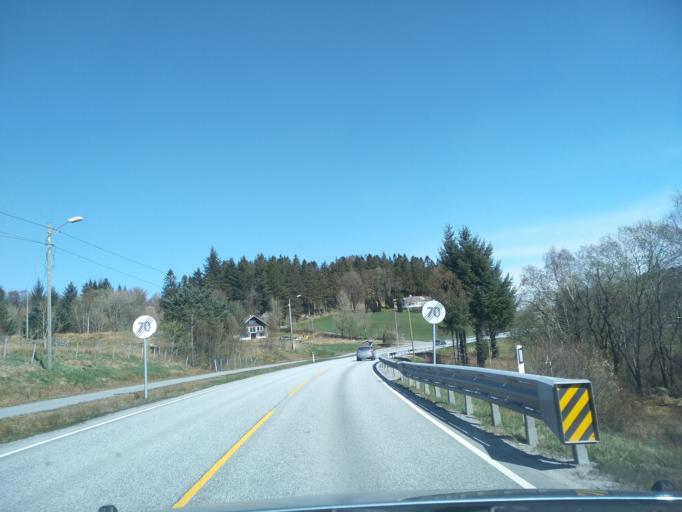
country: NO
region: Rogaland
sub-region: Tysvaer
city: Aksdal
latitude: 59.4694
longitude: 5.5141
